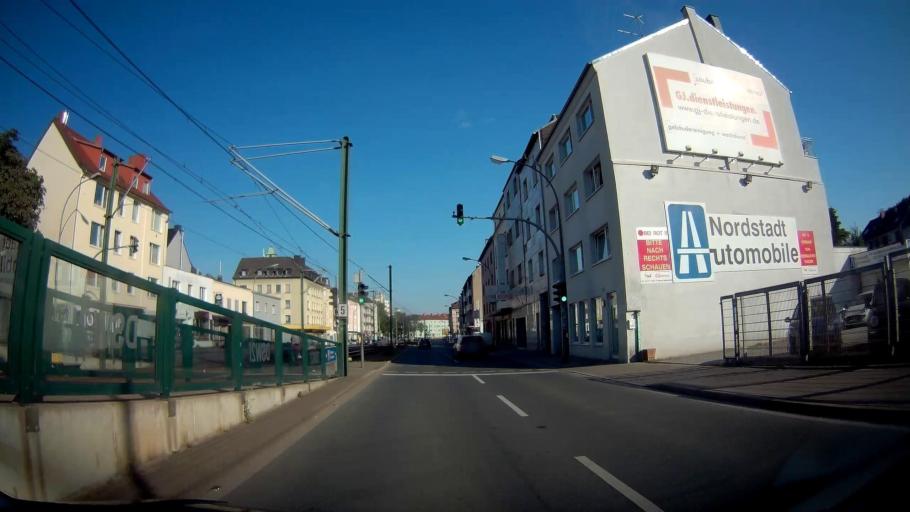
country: DE
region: North Rhine-Westphalia
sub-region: Regierungsbezirk Arnsberg
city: Dortmund
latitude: 51.5292
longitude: 7.4604
